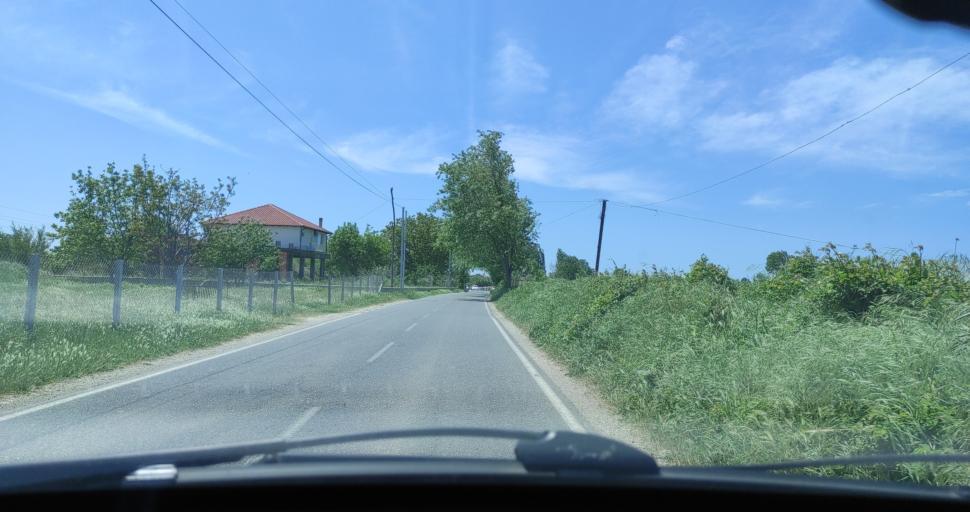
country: AL
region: Lezhe
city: Lezhe
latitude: 41.7621
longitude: 19.6314
